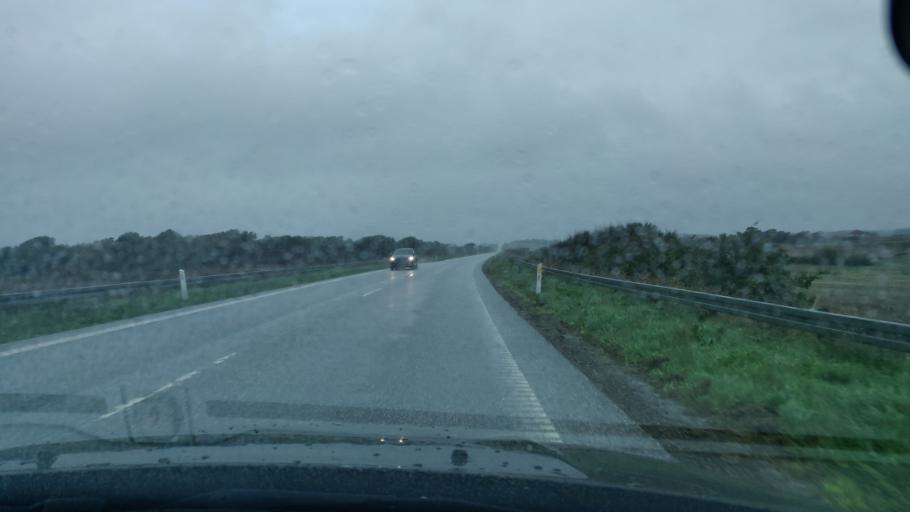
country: DK
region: North Denmark
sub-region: Thisted Kommune
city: Hurup
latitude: 56.8009
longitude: 8.4735
